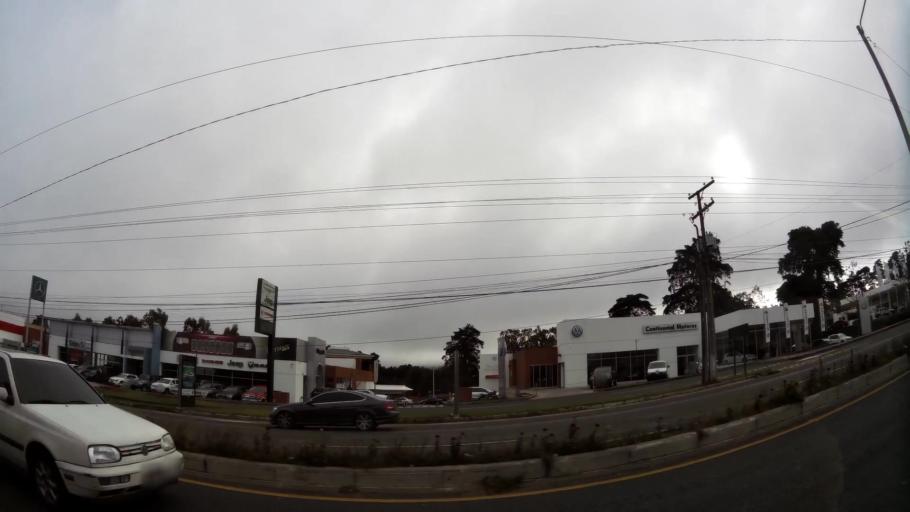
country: GT
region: Guatemala
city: San Jose Pinula
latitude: 14.5474
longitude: -90.4550
